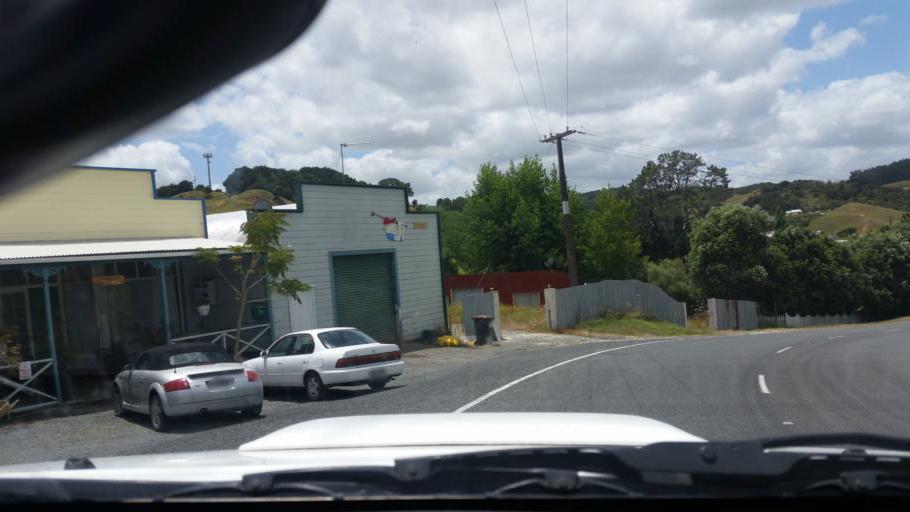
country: NZ
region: Northland
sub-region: Whangarei
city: Ruakaka
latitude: -36.0978
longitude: 174.2397
